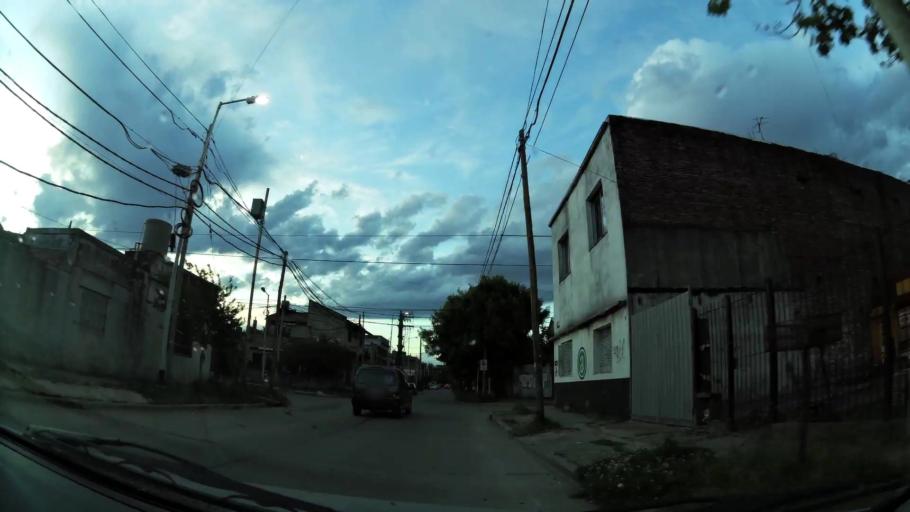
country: AR
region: Buenos Aires
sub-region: Partido de Avellaneda
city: Avellaneda
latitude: -34.6809
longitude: -58.3364
